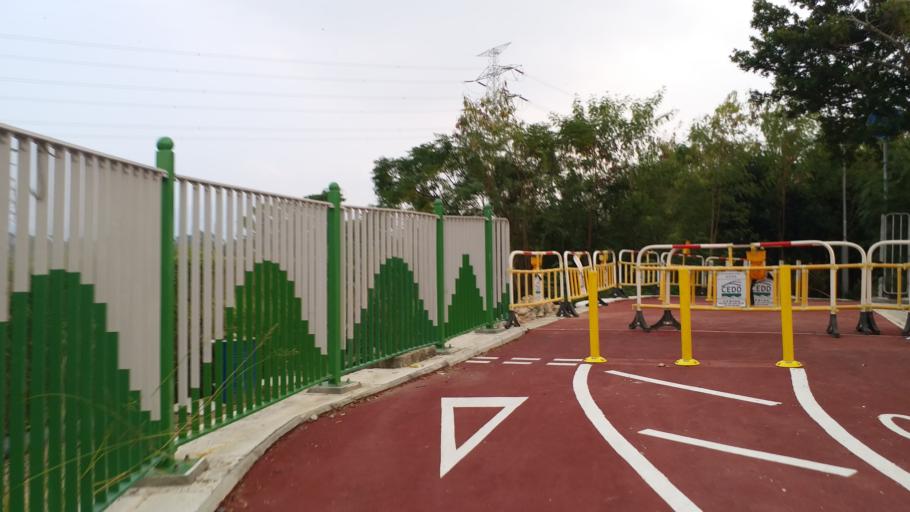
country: HK
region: Yuen Long
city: Yuen Long Kau Hui
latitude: 22.4603
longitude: 114.0468
